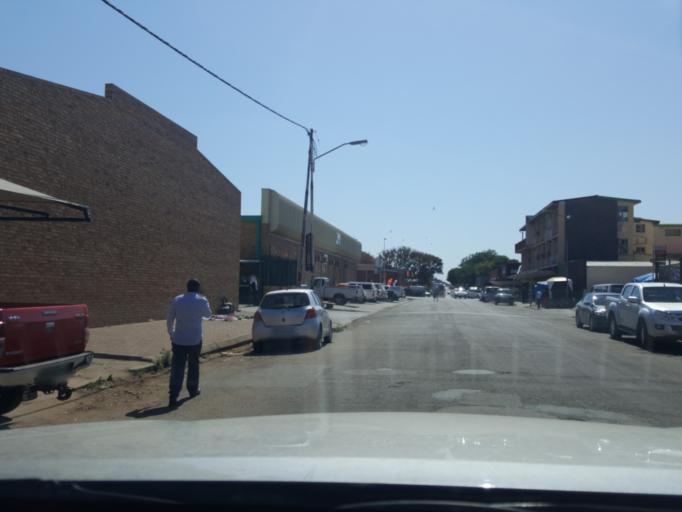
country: ZA
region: North-West
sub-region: Ngaka Modiri Molema District Municipality
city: Zeerust
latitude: -25.5445
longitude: 26.0776
